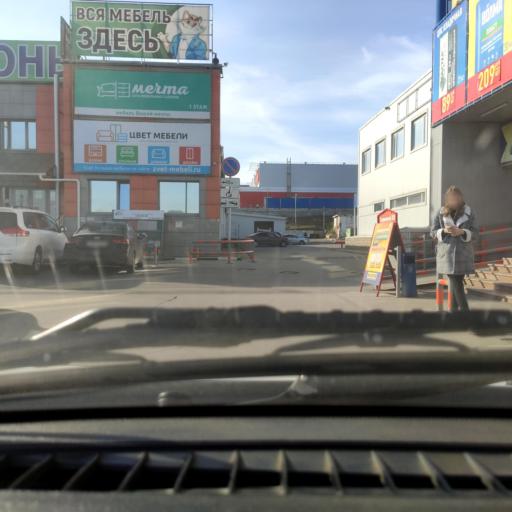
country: RU
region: Samara
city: Zhigulevsk
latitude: 53.4871
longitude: 49.4854
